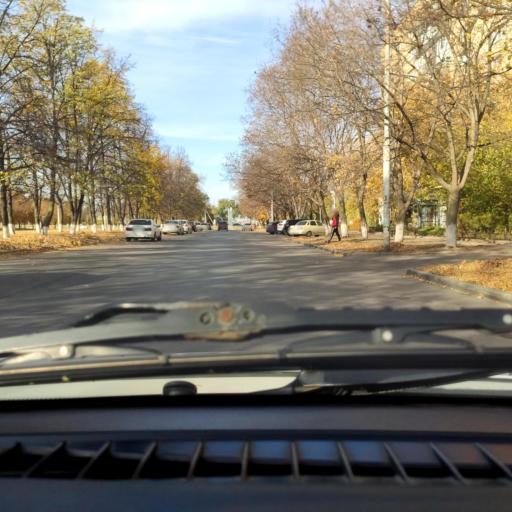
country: RU
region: Samara
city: Tol'yatti
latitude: 53.5217
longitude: 49.2629
